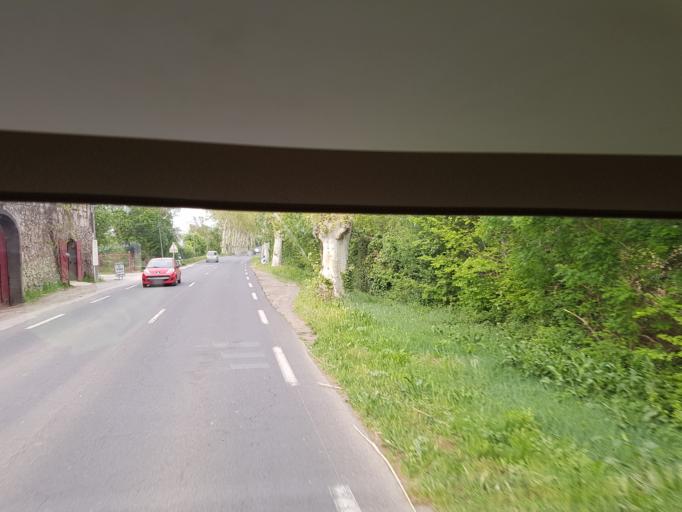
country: FR
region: Languedoc-Roussillon
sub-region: Departement de l'Herault
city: Agde
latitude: 43.3226
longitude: 3.4773
